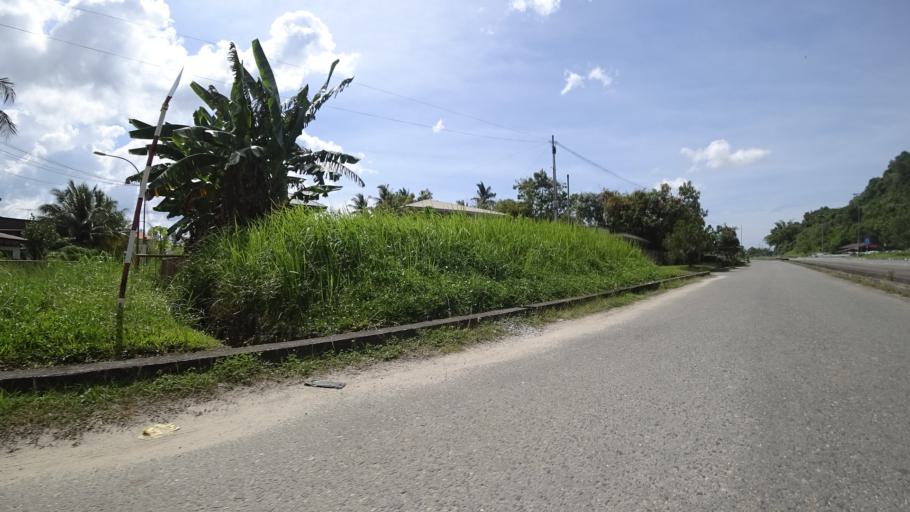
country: BN
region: Brunei and Muara
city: Bandar Seri Begawan
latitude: 4.8531
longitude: 114.8748
